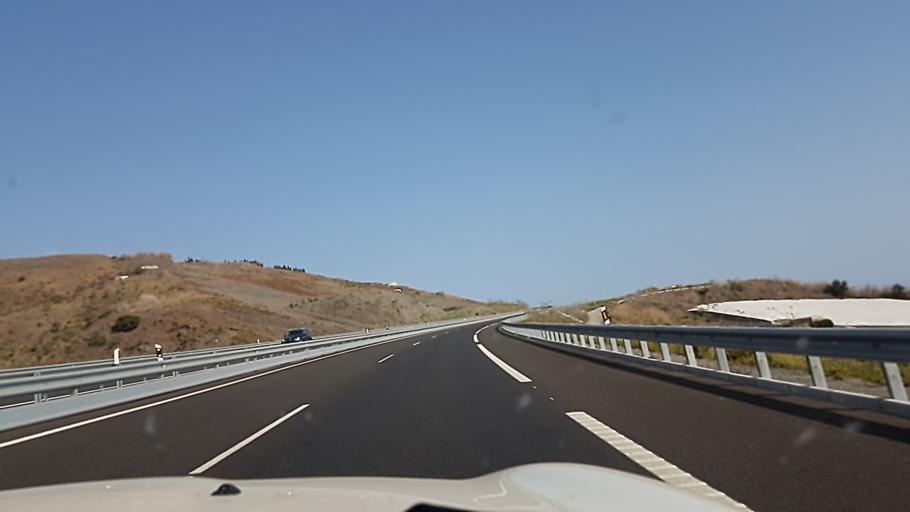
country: ES
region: Andalusia
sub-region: Provincia de Granada
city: Albunol
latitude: 36.7550
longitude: -3.2208
